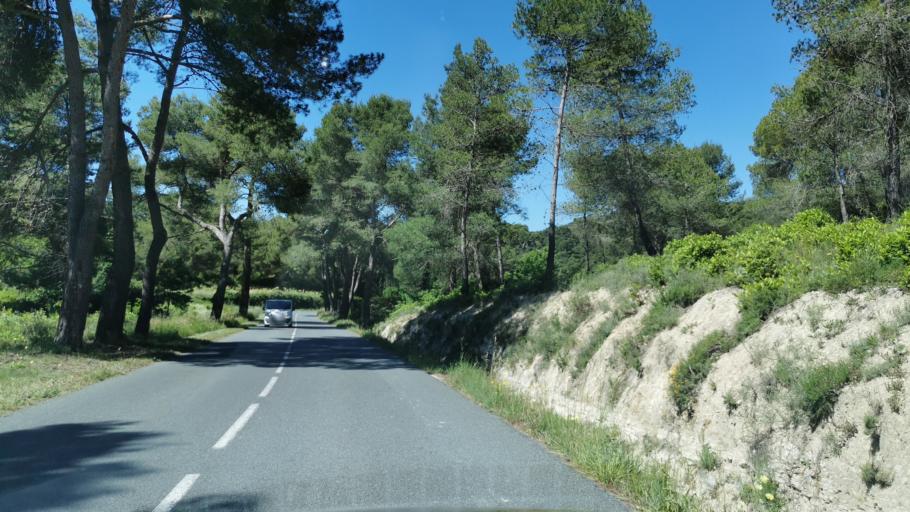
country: FR
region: Languedoc-Roussillon
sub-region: Departement de l'Aude
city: Armissan
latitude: 43.1748
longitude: 3.0801
